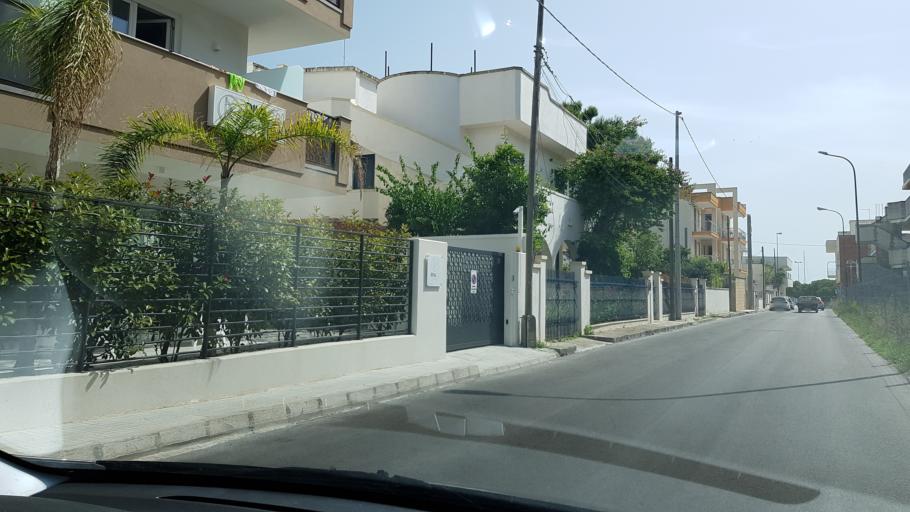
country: IT
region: Apulia
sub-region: Provincia di Lecce
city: Porto Cesareo
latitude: 40.2636
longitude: 17.8896
